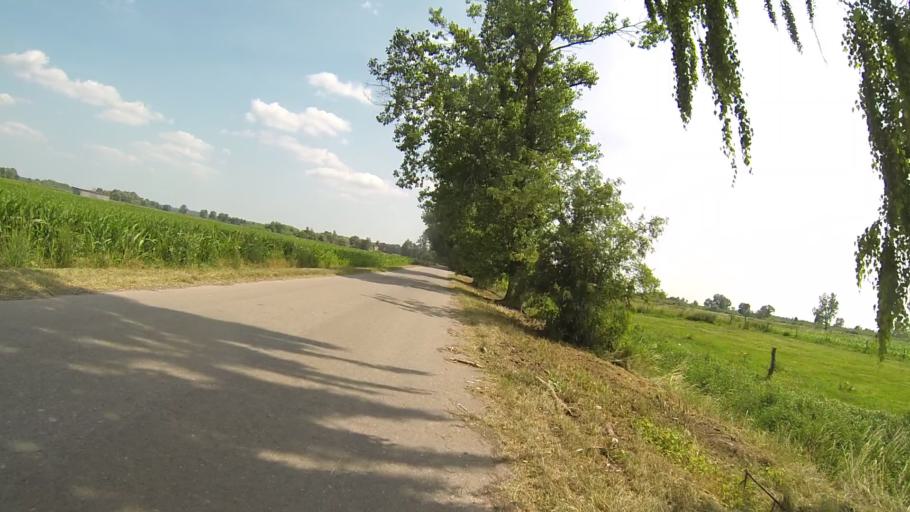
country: DE
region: Baden-Wuerttemberg
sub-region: Regierungsbezirk Stuttgart
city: Niederstotzingen
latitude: 48.5074
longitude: 10.2628
